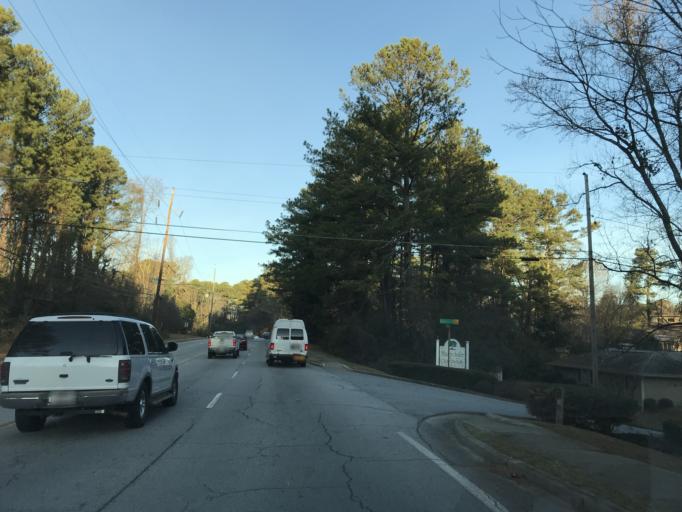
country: US
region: Georgia
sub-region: DeKalb County
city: Tucker
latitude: 33.8828
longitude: -84.2321
